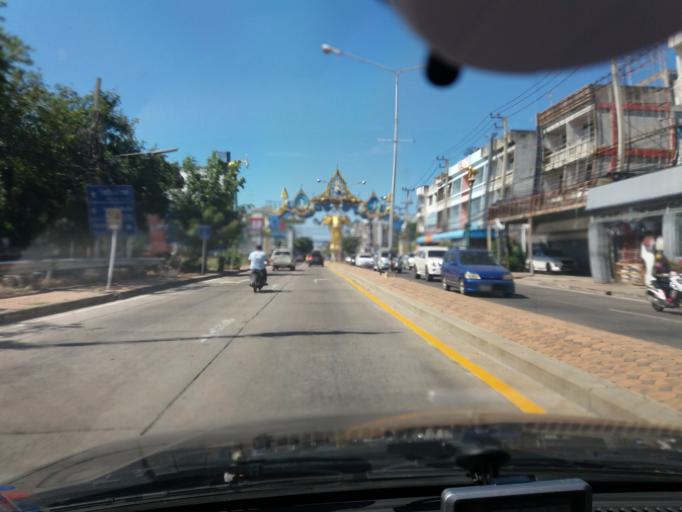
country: TH
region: Suphan Buri
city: Suphan Buri
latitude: 14.4662
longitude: 100.1262
